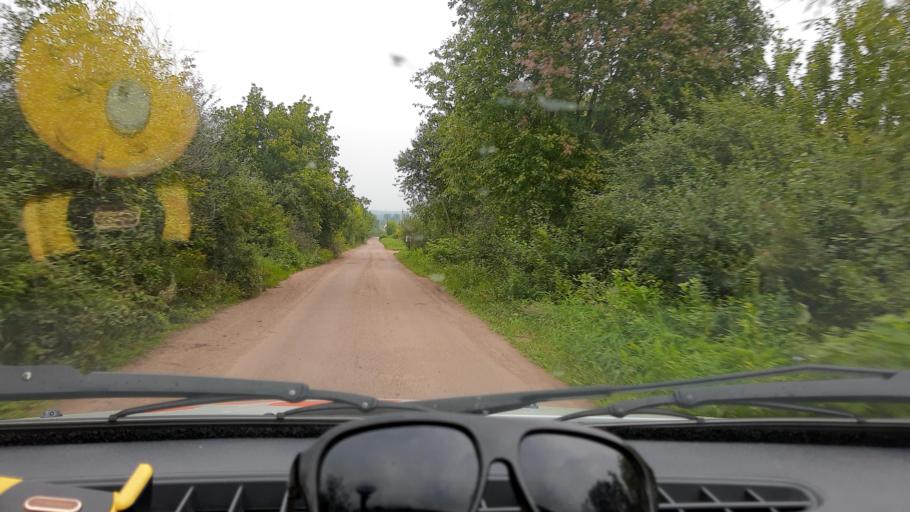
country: RU
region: Bashkortostan
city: Asanovo
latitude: 54.9866
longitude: 55.6132
